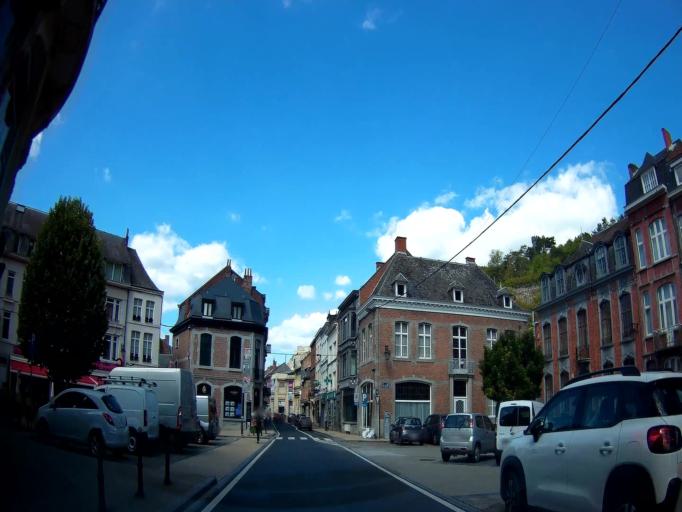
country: BE
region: Wallonia
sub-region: Province de Namur
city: Dinant
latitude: 50.2560
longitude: 4.9163
